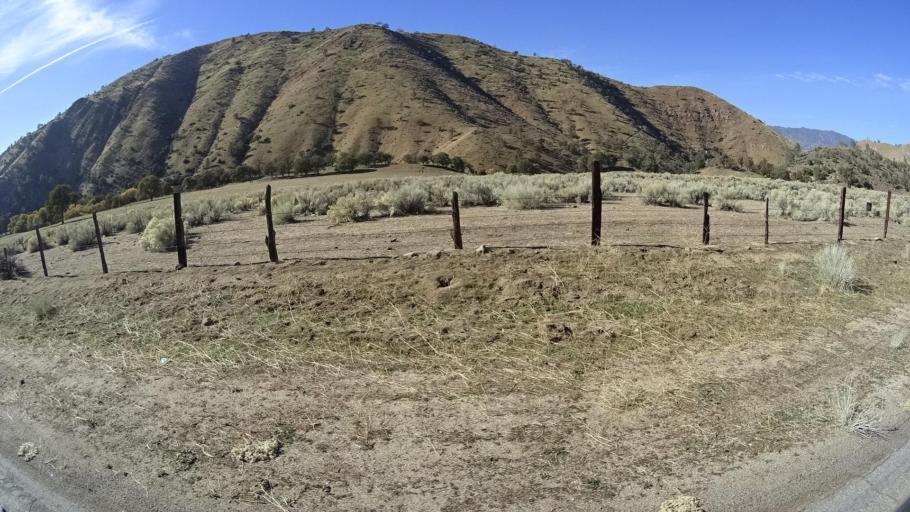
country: US
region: California
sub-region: Kern County
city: Bodfish
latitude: 35.5414
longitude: -118.5094
